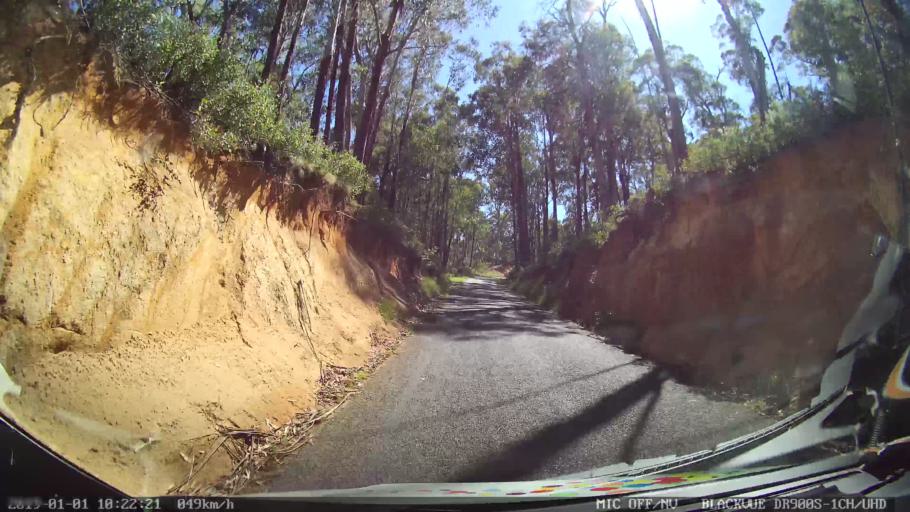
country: AU
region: New South Wales
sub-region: Snowy River
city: Jindabyne
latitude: -36.0783
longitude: 148.2030
